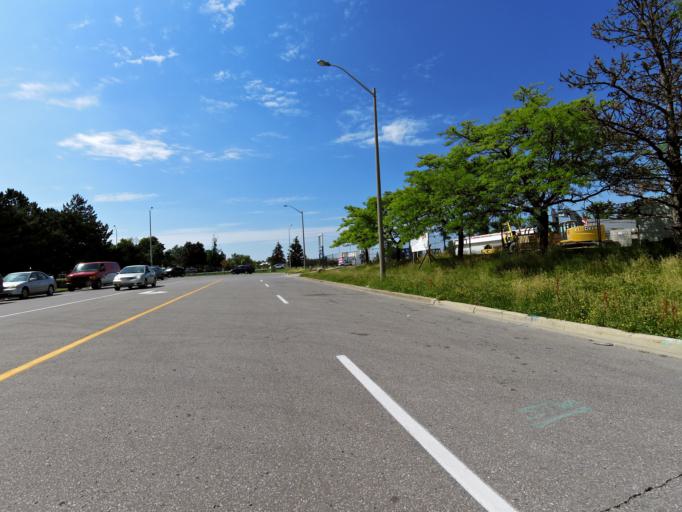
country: CA
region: Ontario
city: Brampton
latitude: 43.7217
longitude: -79.7190
